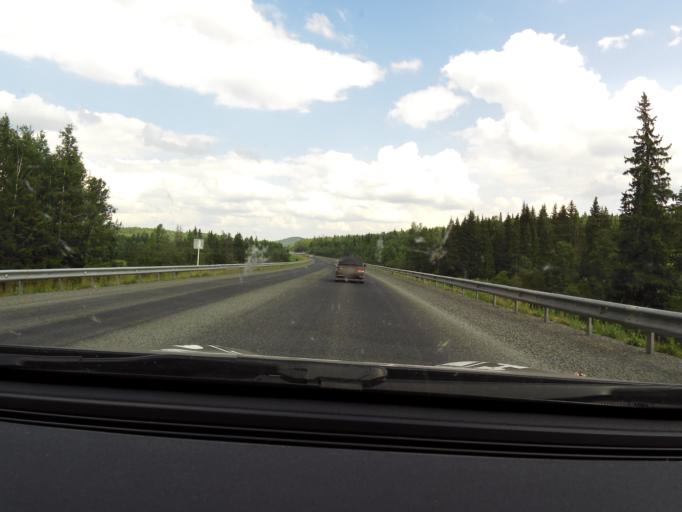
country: RU
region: Sverdlovsk
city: Arti
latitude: 56.7886
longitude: 58.5740
